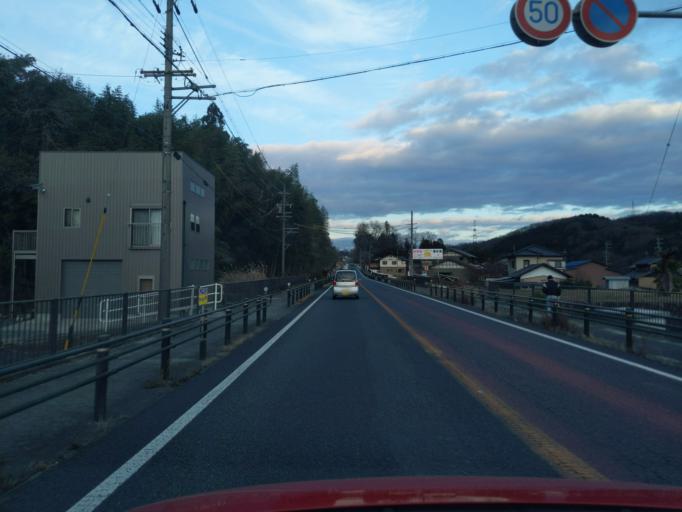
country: JP
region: Gifu
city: Mizunami
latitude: 35.4158
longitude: 137.3109
